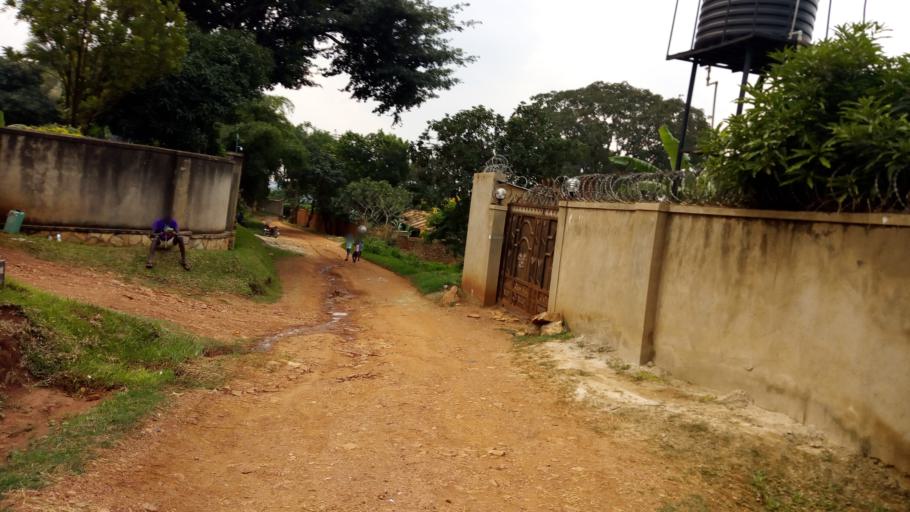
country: UG
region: Central Region
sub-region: Wakiso District
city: Kireka
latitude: 0.3272
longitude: 32.6344
